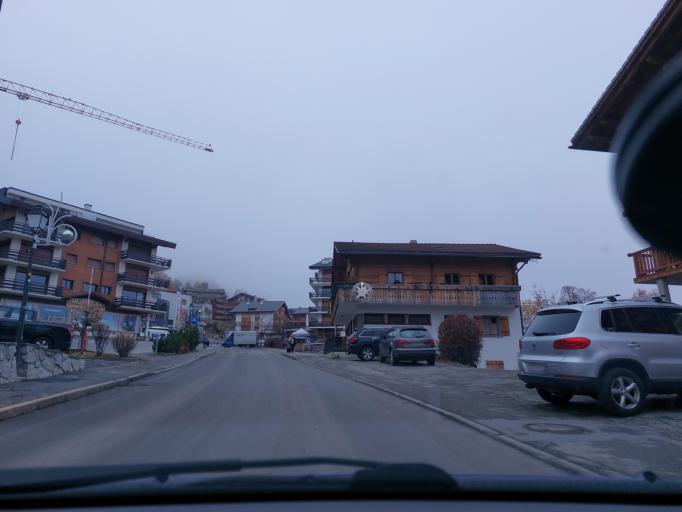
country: CH
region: Valais
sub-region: Conthey District
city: Basse-Nendaz
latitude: 46.1812
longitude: 7.2928
